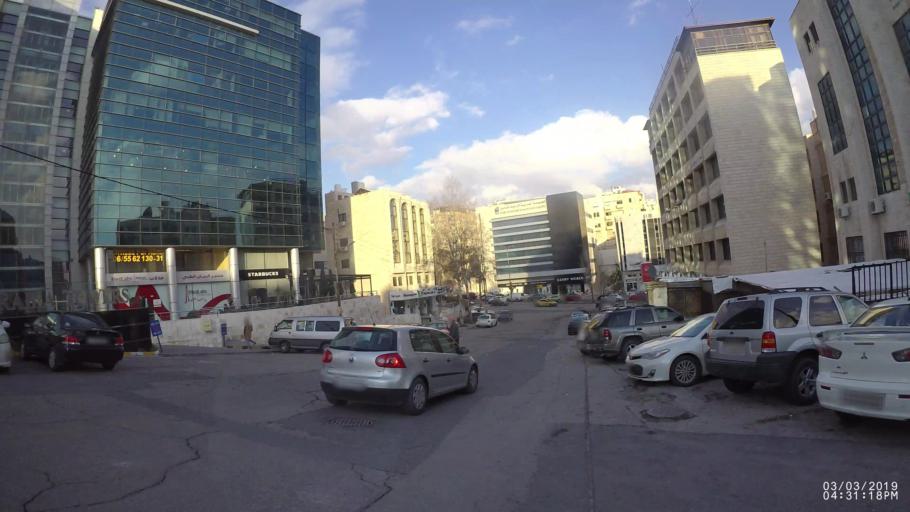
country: JO
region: Amman
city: Al Jubayhah
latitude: 31.9741
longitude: 35.8858
